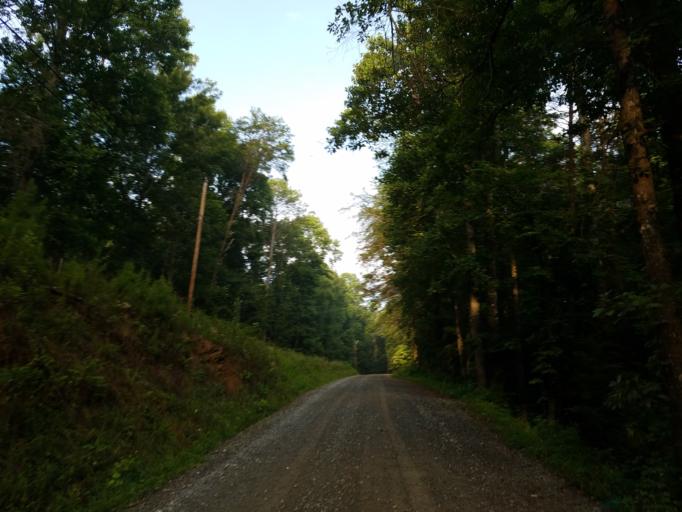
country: US
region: Georgia
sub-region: Pickens County
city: Jasper
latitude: 34.5484
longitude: -84.4415
